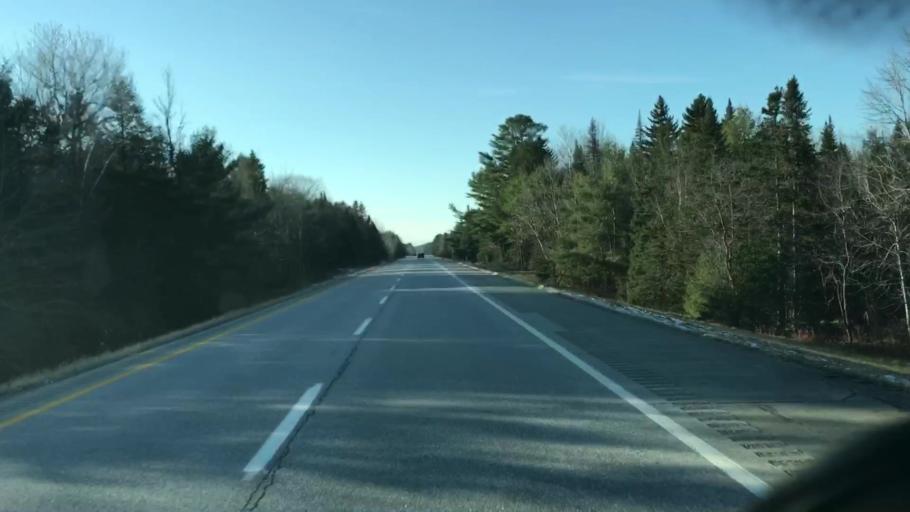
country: US
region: Maine
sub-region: Penobscot County
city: Carmel
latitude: 44.7796
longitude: -69.0676
